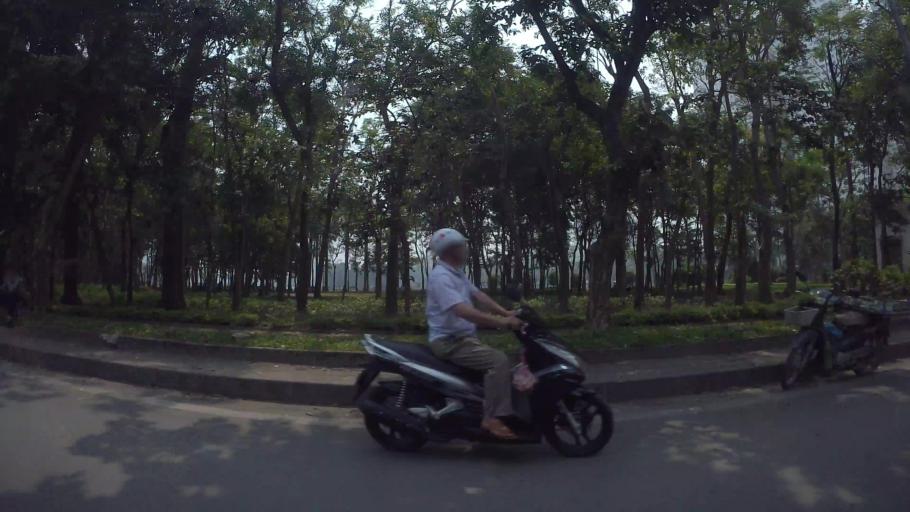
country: VN
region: Ha Noi
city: Van Dien
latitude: 20.9665
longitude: 105.8260
